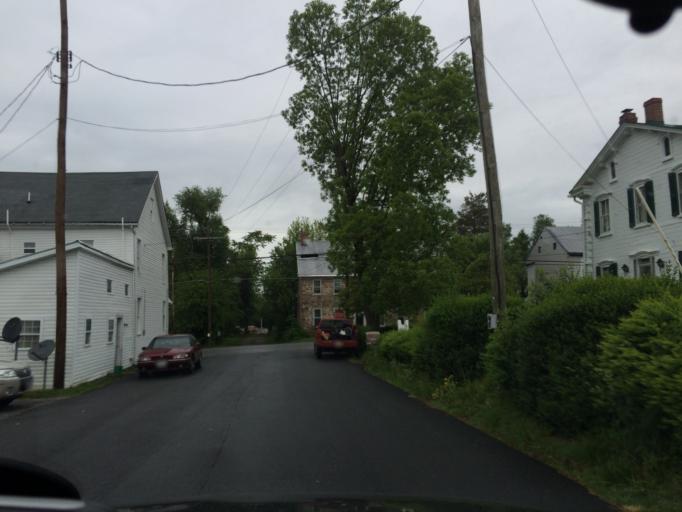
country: US
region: Maryland
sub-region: Carroll County
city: Taneytown
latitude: 39.5945
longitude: -77.2203
